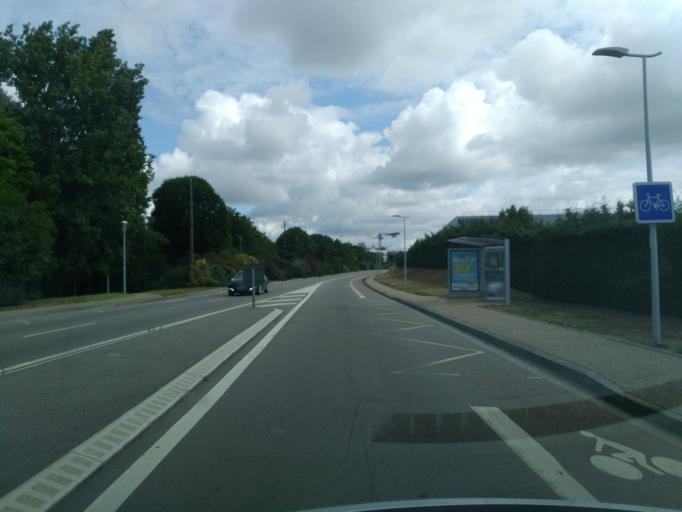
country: FR
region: Ile-de-France
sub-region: Departement des Yvelines
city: Carrieres-sous-Poissy
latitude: 48.9418
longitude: 2.0379
